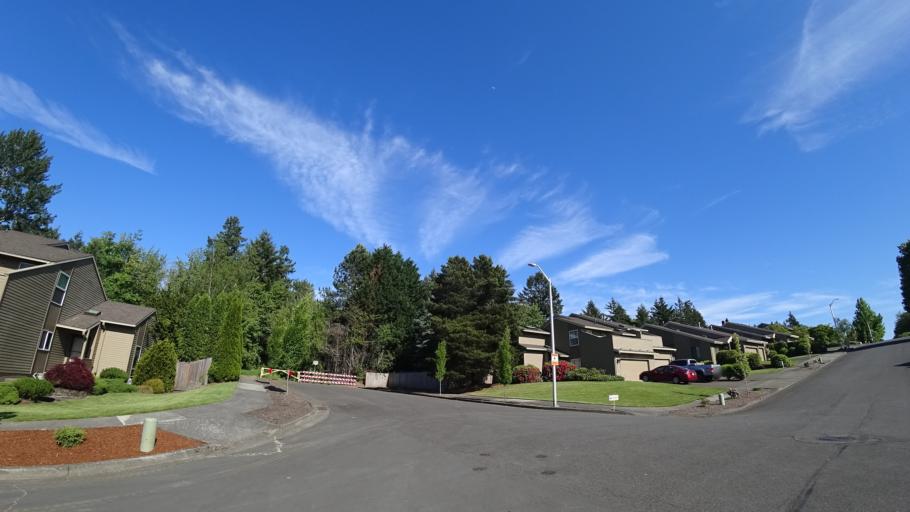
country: US
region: Oregon
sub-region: Washington County
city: Beaverton
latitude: 45.4626
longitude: -122.8066
